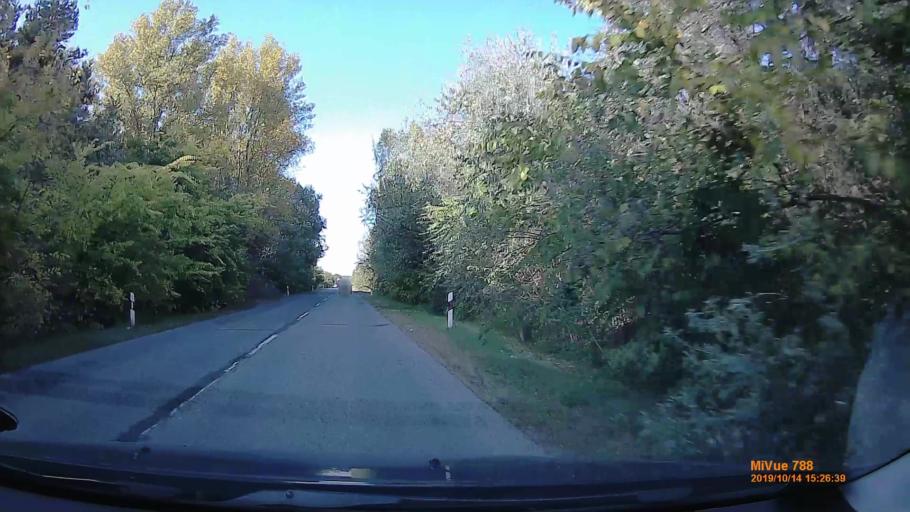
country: HU
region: Pest
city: Ecser
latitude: 47.4213
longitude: 19.3124
